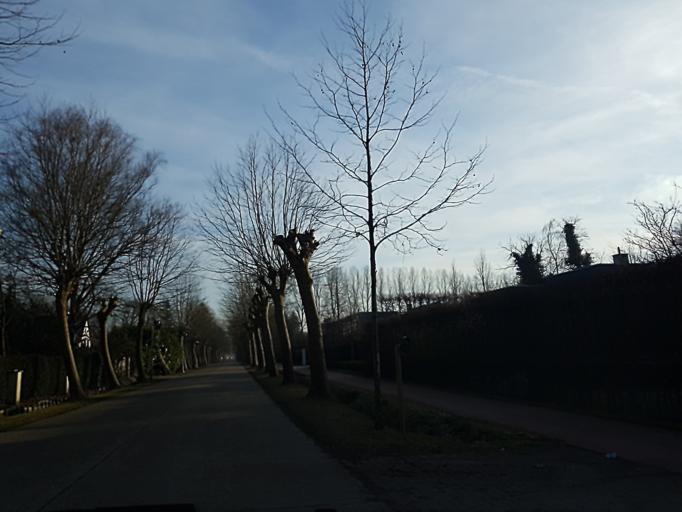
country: BE
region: Flanders
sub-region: Provincie Antwerpen
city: Schilde
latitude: 51.2586
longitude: 4.5954
